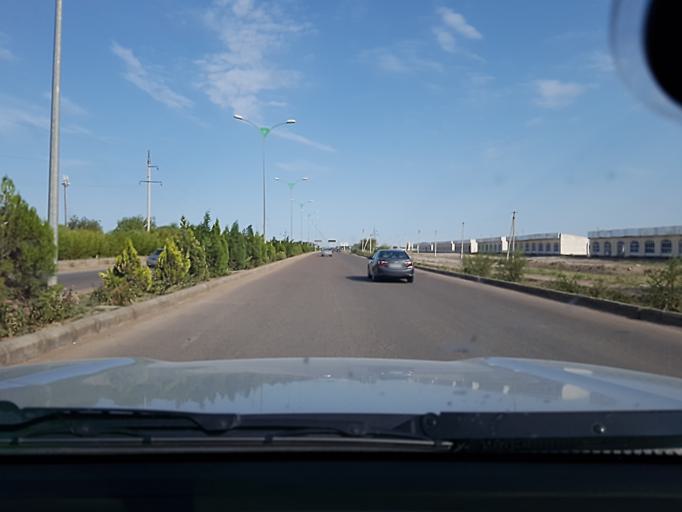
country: TM
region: Dasoguz
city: Koeneuergench
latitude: 42.3169
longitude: 59.1671
